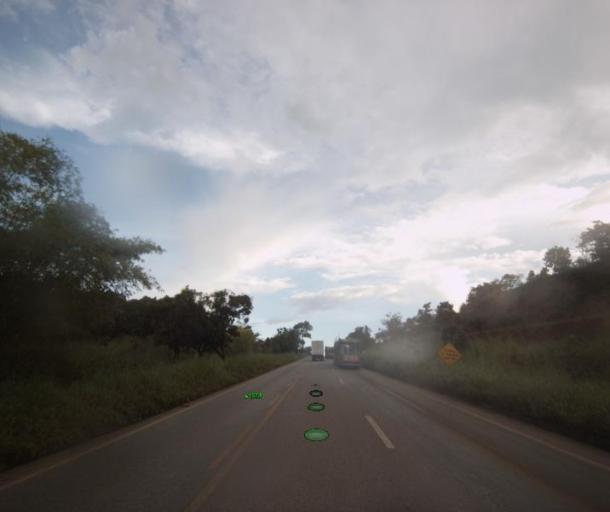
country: BR
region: Goias
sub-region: Porangatu
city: Porangatu
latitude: -13.9780
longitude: -49.0905
